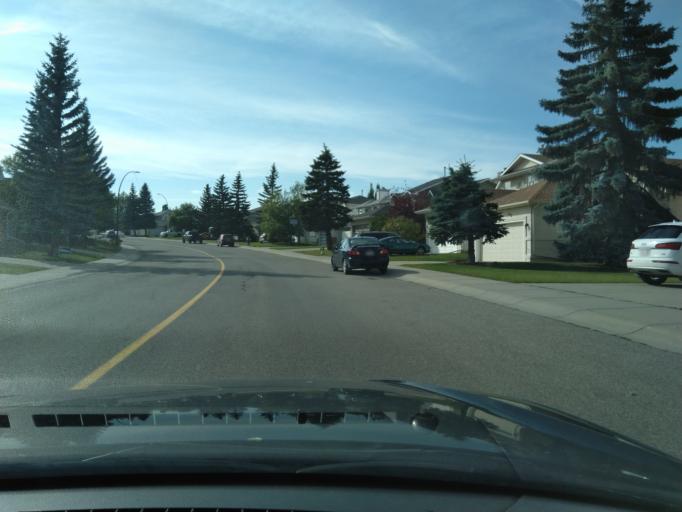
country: CA
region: Alberta
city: Calgary
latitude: 51.1403
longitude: -114.0972
